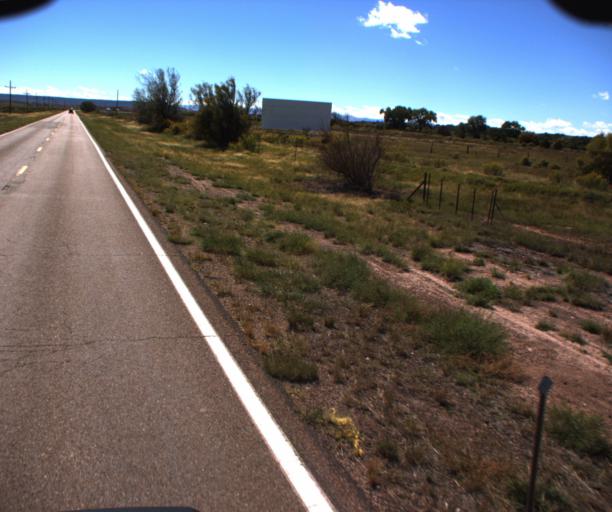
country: US
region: Arizona
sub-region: Apache County
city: Saint Johns
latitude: 34.5174
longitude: -109.3474
